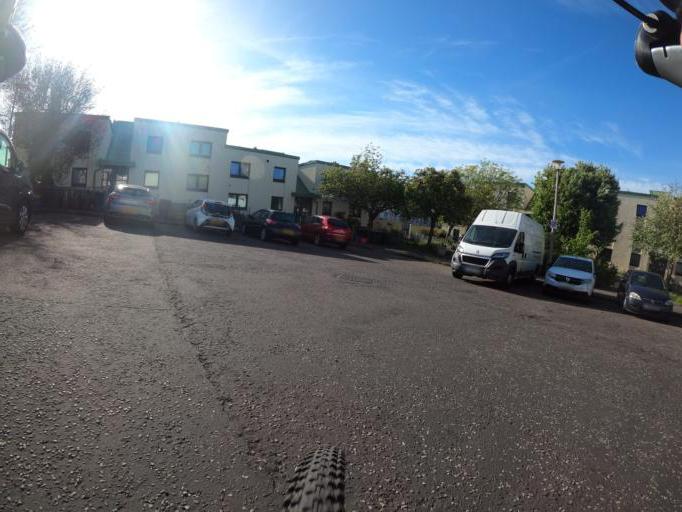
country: GB
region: Scotland
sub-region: Edinburgh
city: Edinburgh
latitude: 55.9796
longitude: -3.2260
